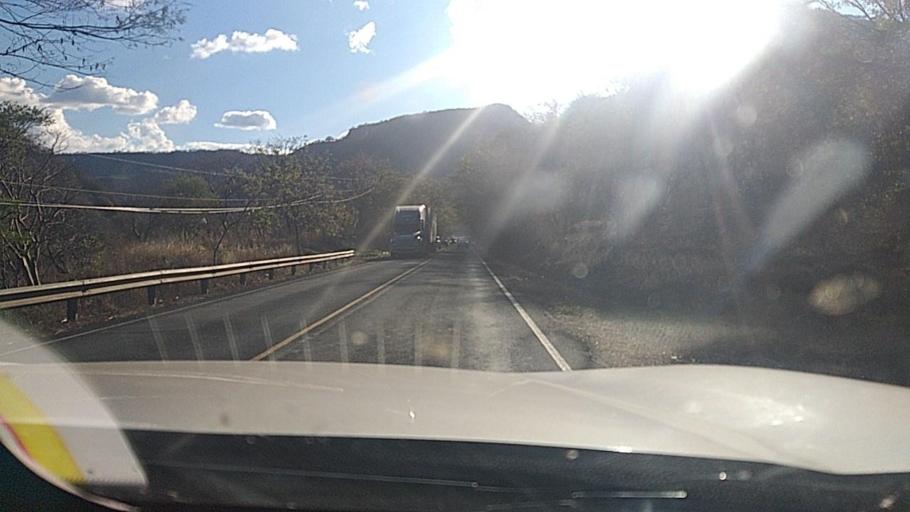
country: NI
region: Esteli
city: Condega
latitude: 13.2789
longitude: -86.3489
